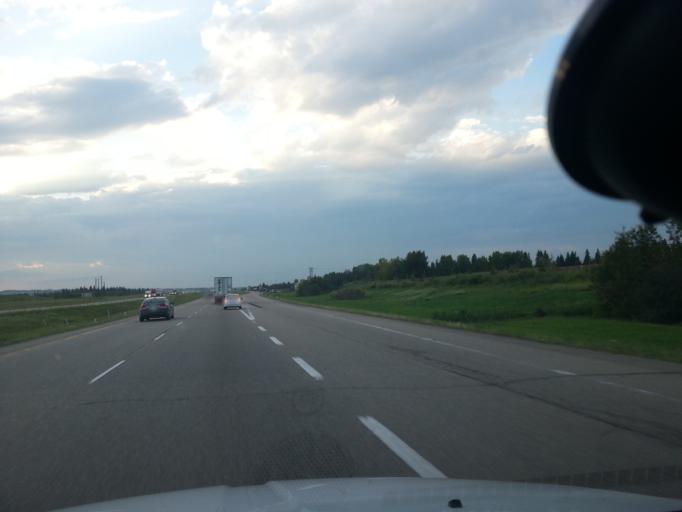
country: CA
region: Alberta
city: Red Deer
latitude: 52.2573
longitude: -113.8504
